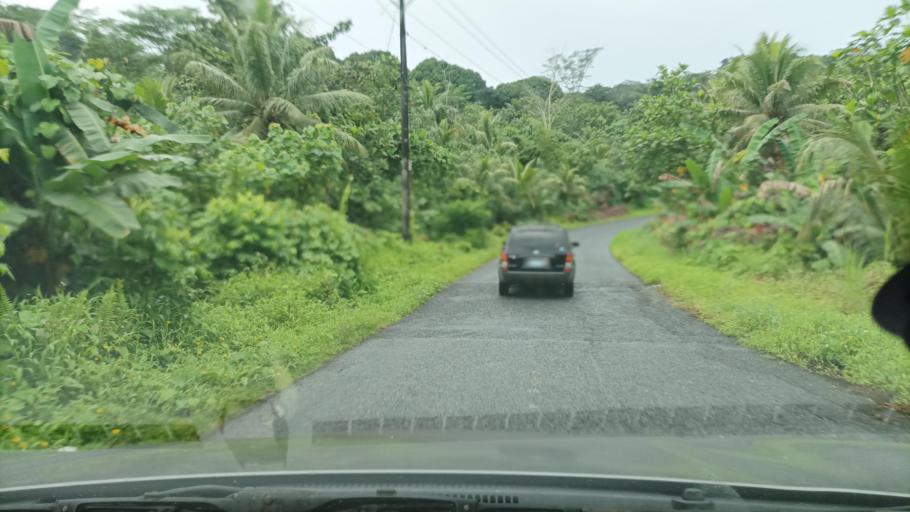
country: FM
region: Pohnpei
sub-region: Sokehs Municipality
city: Palikir - National Government Center
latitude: 6.8961
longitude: 158.1575
